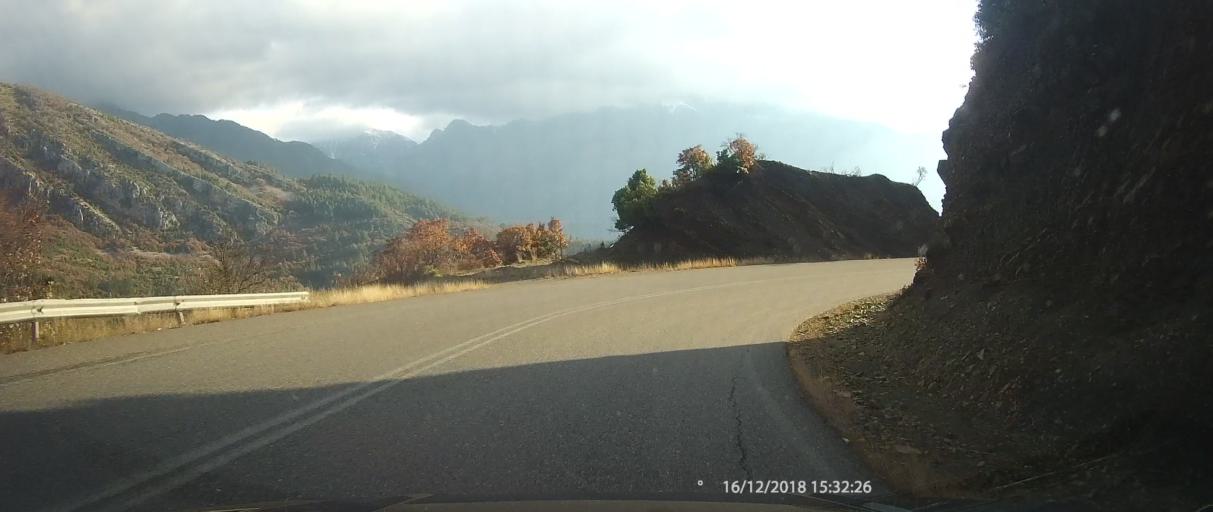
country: GR
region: Epirus
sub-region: Nomos Ioanninon
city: Konitsa
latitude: 40.0693
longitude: 20.7403
